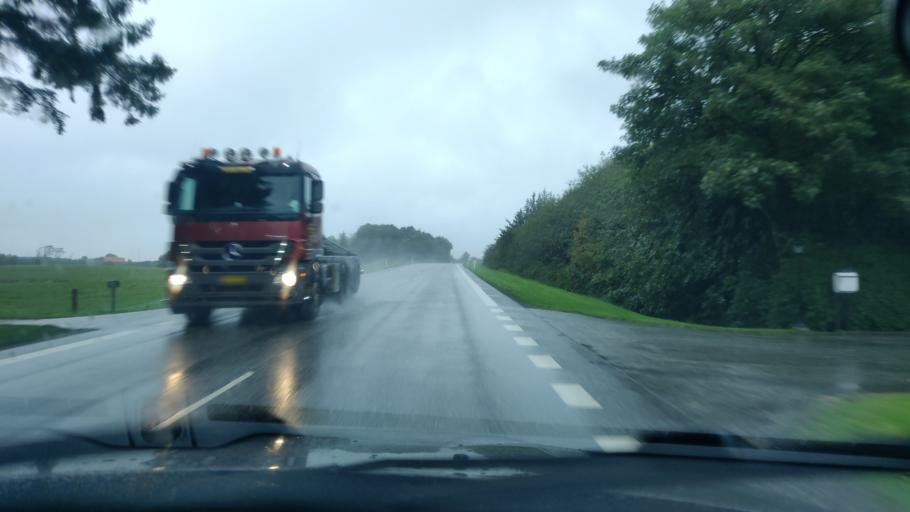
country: DK
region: North Denmark
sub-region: Thisted Kommune
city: Hurup
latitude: 56.8367
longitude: 8.5119
